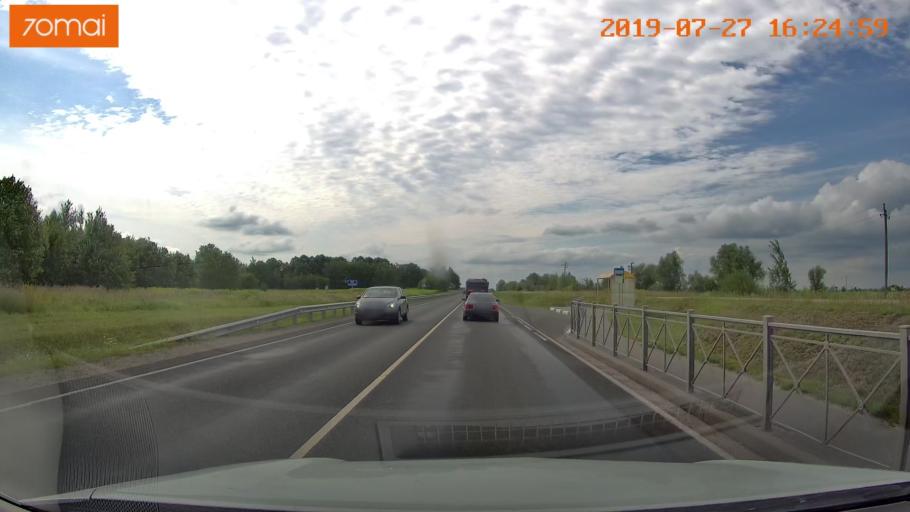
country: RU
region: Kaliningrad
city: Zheleznodorozhnyy
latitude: 54.6358
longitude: 21.4411
